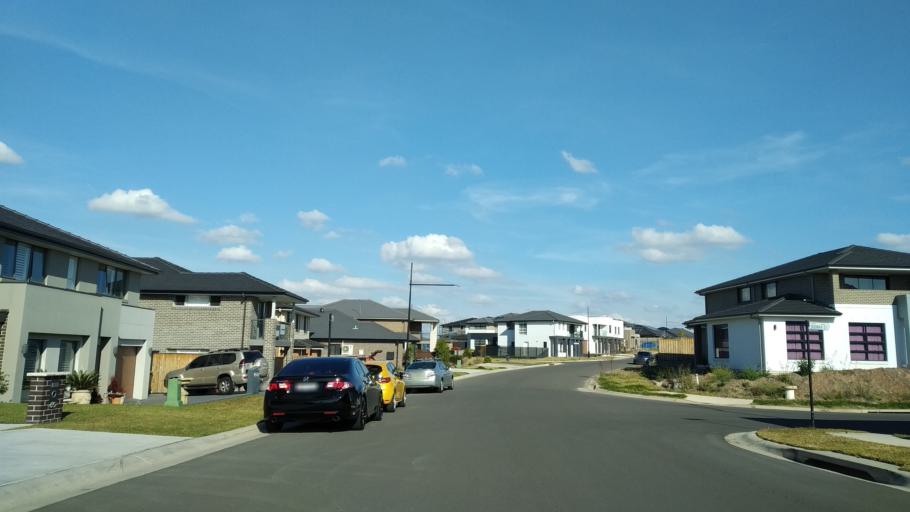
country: AU
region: New South Wales
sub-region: Blacktown
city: Quakers Hill
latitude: -33.7204
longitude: 150.8624
